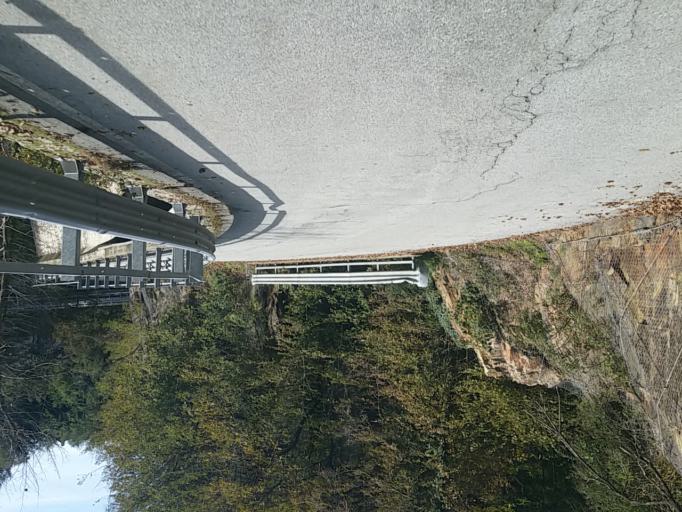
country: IT
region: Piedmont
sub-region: Provincia Verbano-Cusio-Ossola
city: Cavaglio-Spoccia
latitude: 46.0665
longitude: 8.6265
